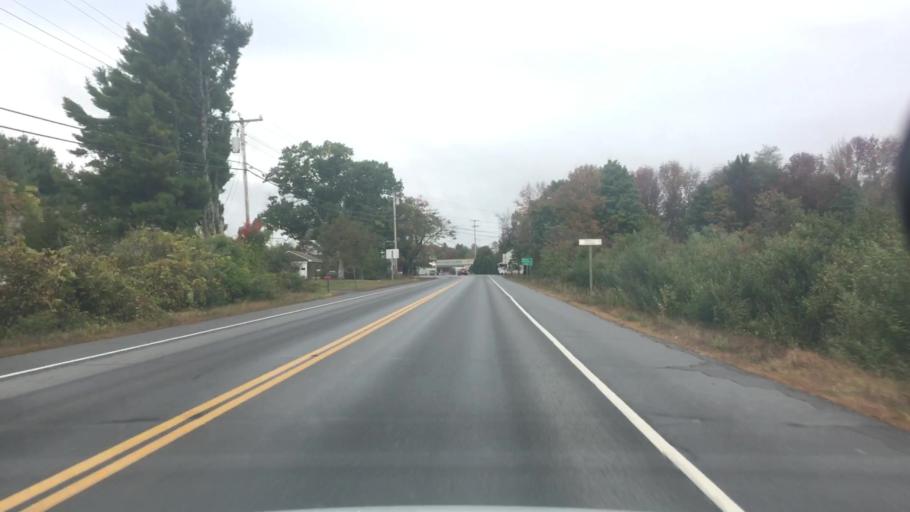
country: US
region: Maine
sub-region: Kennebec County
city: Belgrade
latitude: 44.3934
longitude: -69.8027
